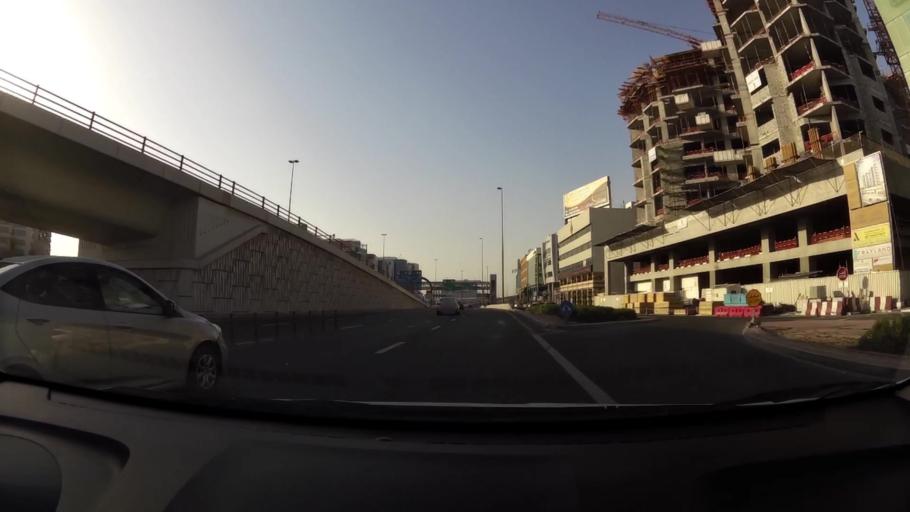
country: AE
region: Ash Shariqah
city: Sharjah
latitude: 25.2504
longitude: 55.3368
